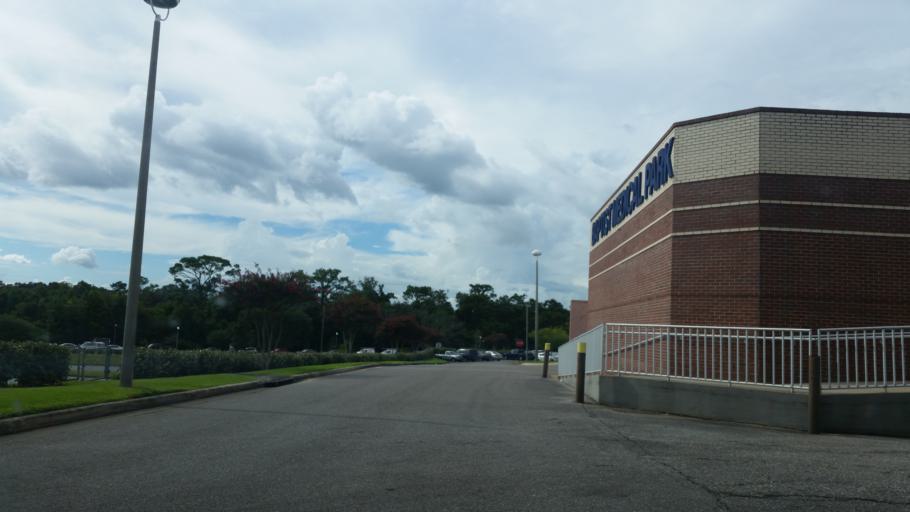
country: US
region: Florida
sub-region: Escambia County
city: Ferry Pass
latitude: 30.5328
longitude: -87.2197
